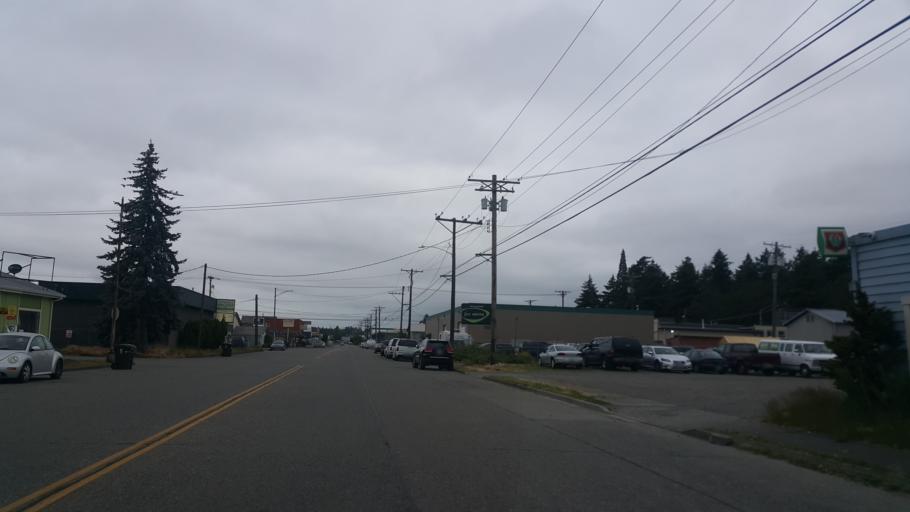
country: US
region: Washington
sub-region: Pierce County
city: Fircrest
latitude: 47.2103
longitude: -122.4851
